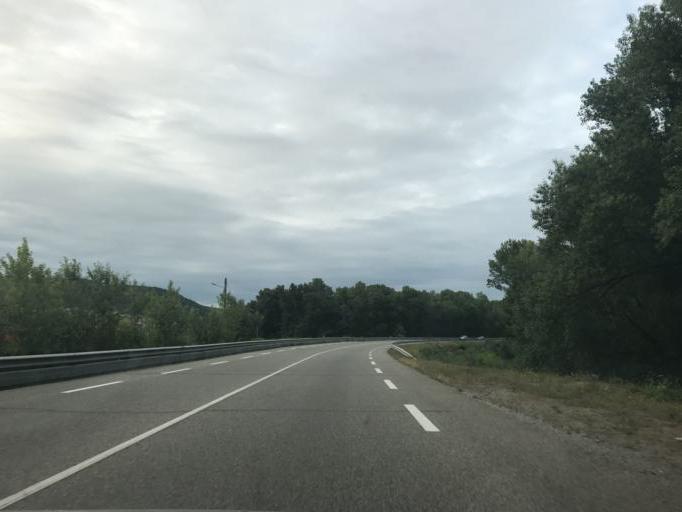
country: FR
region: Rhone-Alpes
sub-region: Departement de l'Ardeche
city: Beauchastel
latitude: 44.8103
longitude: 4.7973
